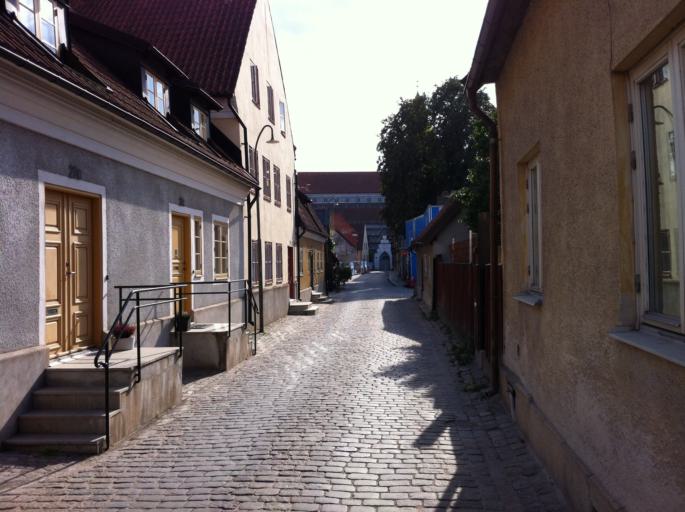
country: SE
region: Gotland
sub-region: Gotland
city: Visby
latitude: 57.6434
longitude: 18.2992
